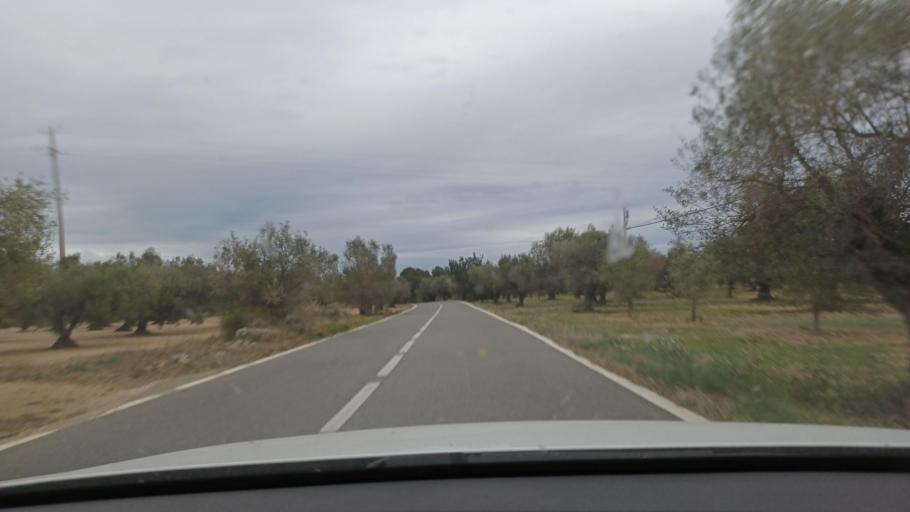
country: ES
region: Catalonia
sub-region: Provincia de Tarragona
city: Ulldecona
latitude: 40.6177
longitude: 0.3584
